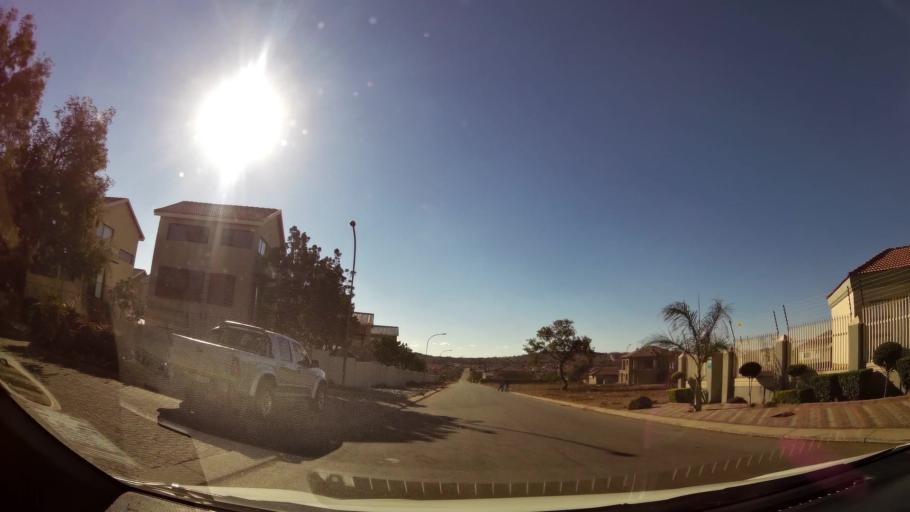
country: ZA
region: Limpopo
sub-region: Capricorn District Municipality
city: Polokwane
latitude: -23.9085
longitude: 29.5031
